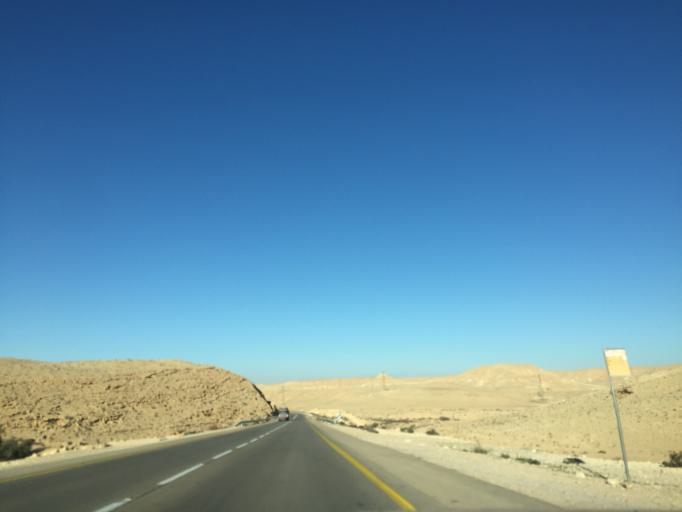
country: IL
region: Southern District
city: Midreshet Ben-Gurion
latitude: 30.7542
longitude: 34.7705
